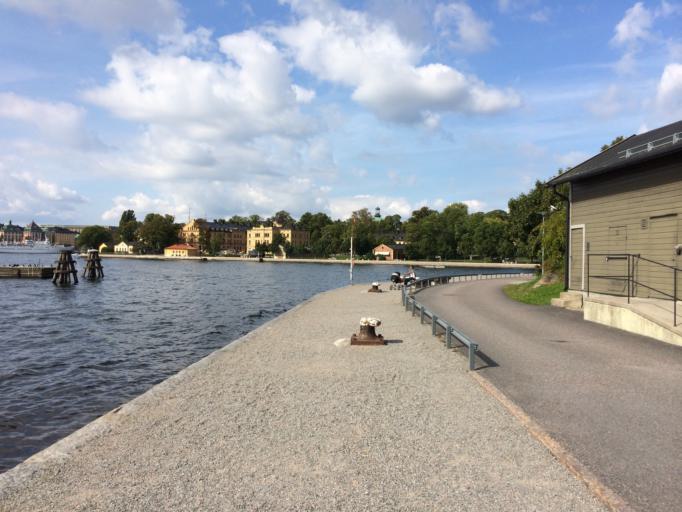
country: SE
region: Stockholm
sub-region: Stockholms Kommun
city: OEstermalm
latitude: 59.3222
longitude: 18.0883
